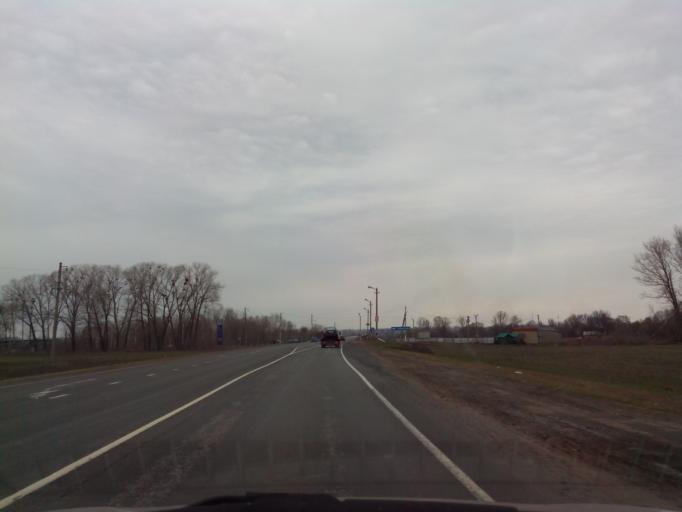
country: RU
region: Tambov
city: Zavoronezhskoye
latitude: 52.9522
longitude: 40.5818
